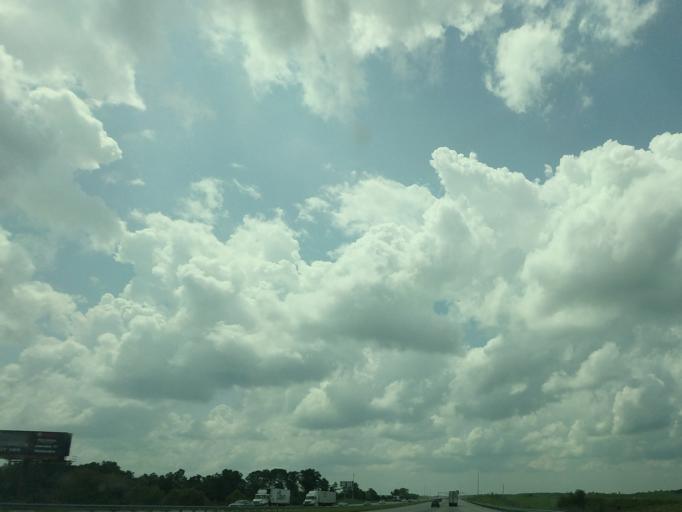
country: US
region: Georgia
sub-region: Peach County
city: Byron
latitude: 32.7280
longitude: -83.7260
